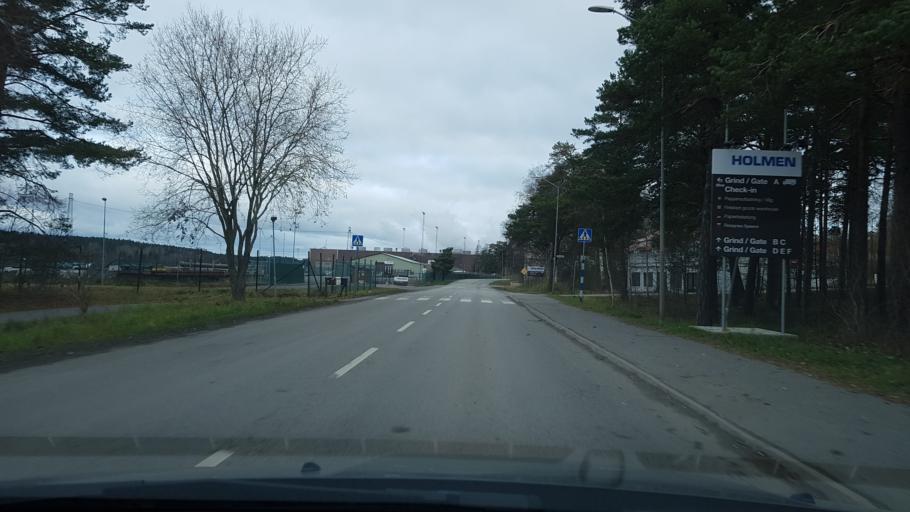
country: SE
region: Stockholm
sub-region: Norrtalje Kommun
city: Hallstavik
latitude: 60.0536
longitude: 18.5948
